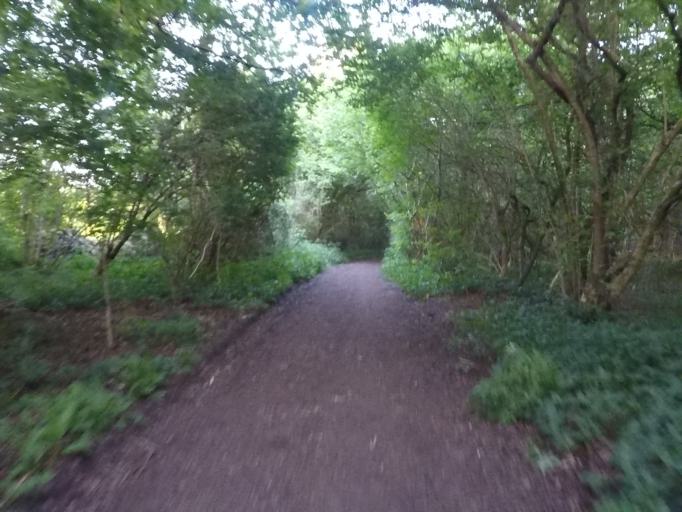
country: GB
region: England
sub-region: Oxfordshire
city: Charlbury
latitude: 51.8328
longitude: -1.5219
